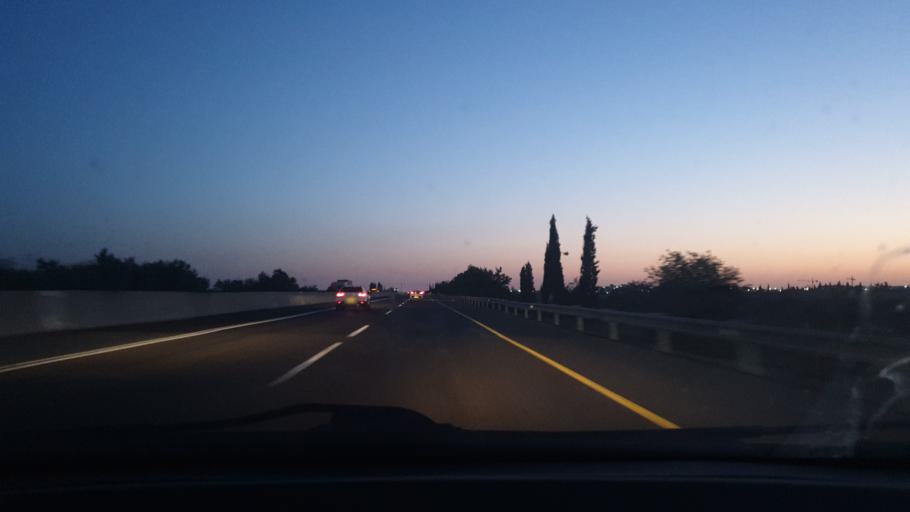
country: IL
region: Central District
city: Gedera
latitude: 31.8020
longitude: 34.8103
